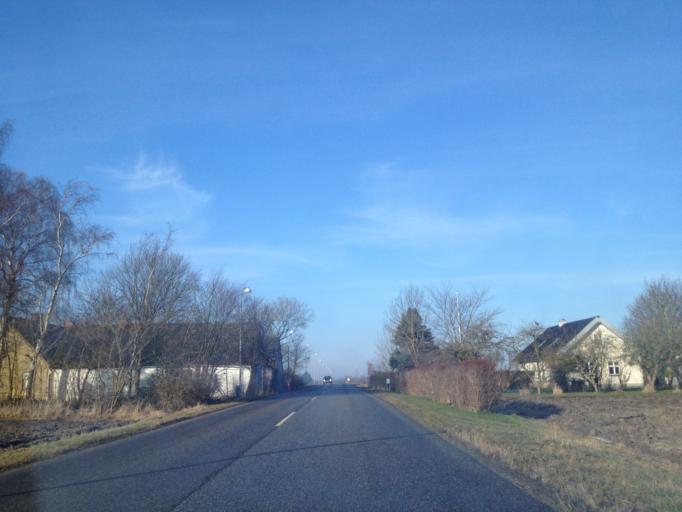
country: DK
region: Zealand
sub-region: Greve Kommune
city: Greve
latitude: 55.6081
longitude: 12.2830
